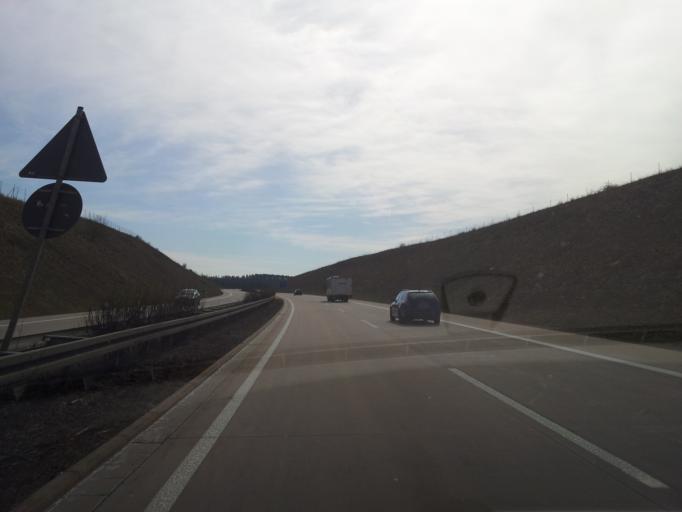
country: DE
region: Thuringia
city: Rohr
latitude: 50.5908
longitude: 10.4912
